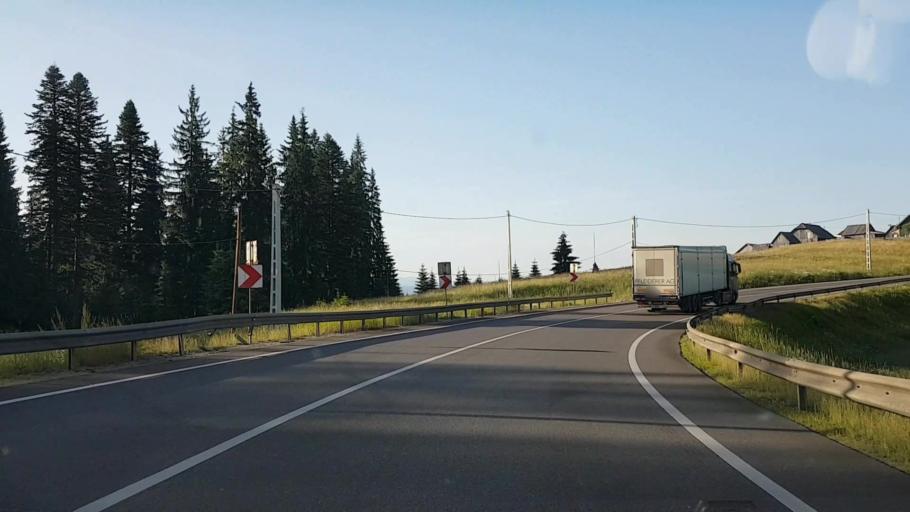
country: RO
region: Suceava
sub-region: Comuna Poiana Stampei
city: Poiana Stampei
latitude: 47.2913
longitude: 25.0767
